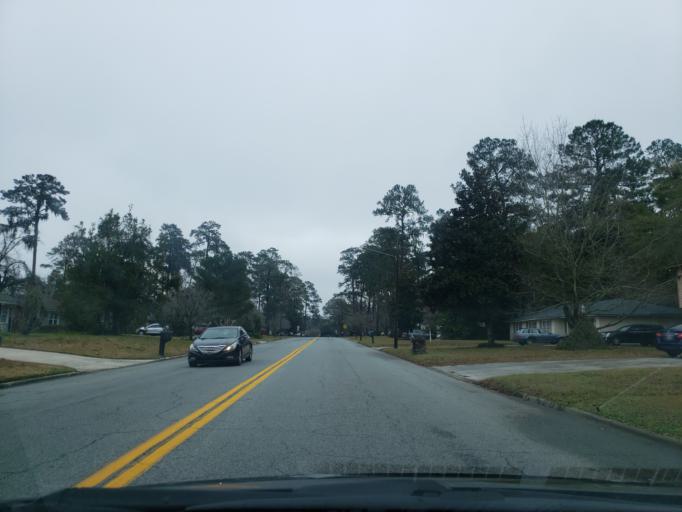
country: US
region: Georgia
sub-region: Chatham County
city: Montgomery
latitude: 31.9729
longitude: -81.1559
